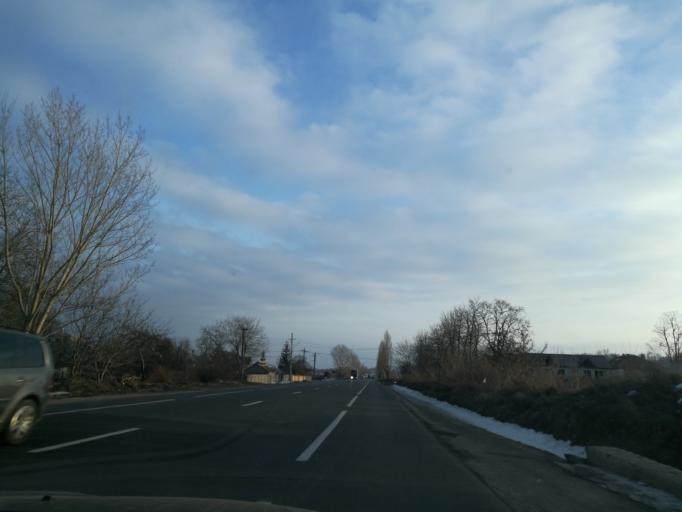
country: RO
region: Bacau
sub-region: Comuna Racaciuni
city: Racaciuni
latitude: 46.3522
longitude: 26.9941
